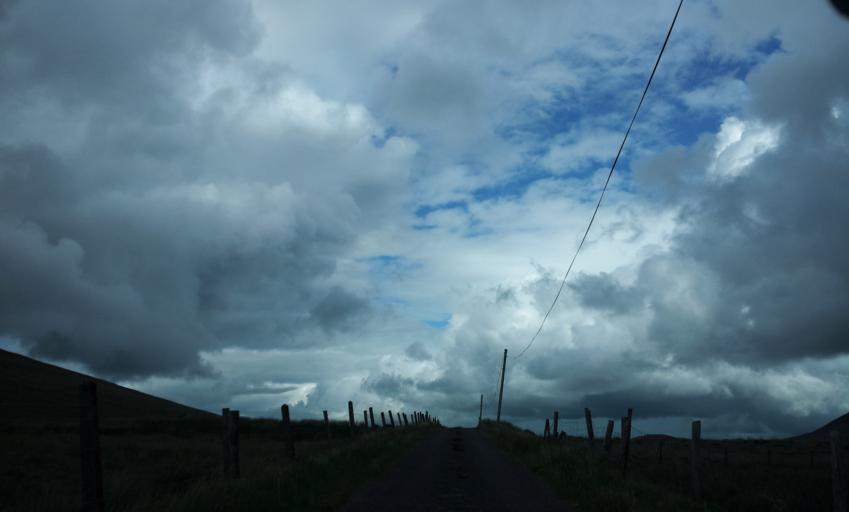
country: IE
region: Munster
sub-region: Ciarrai
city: Killorglin
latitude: 52.1965
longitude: -9.9214
